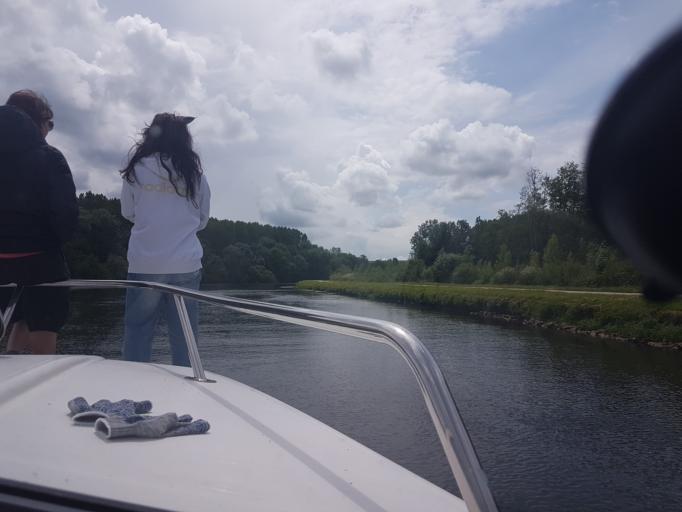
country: FR
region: Bourgogne
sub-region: Departement de l'Yonne
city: Augy
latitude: 47.7780
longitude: 3.6091
